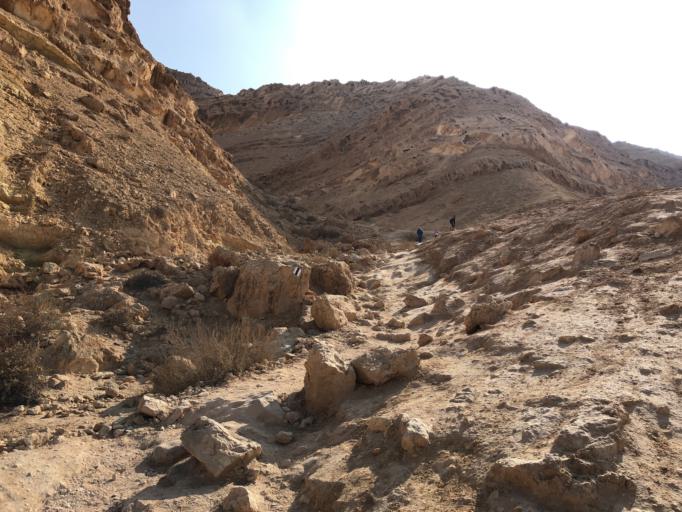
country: IL
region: Southern District
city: Yeroham
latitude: 30.9468
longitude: 35.0250
